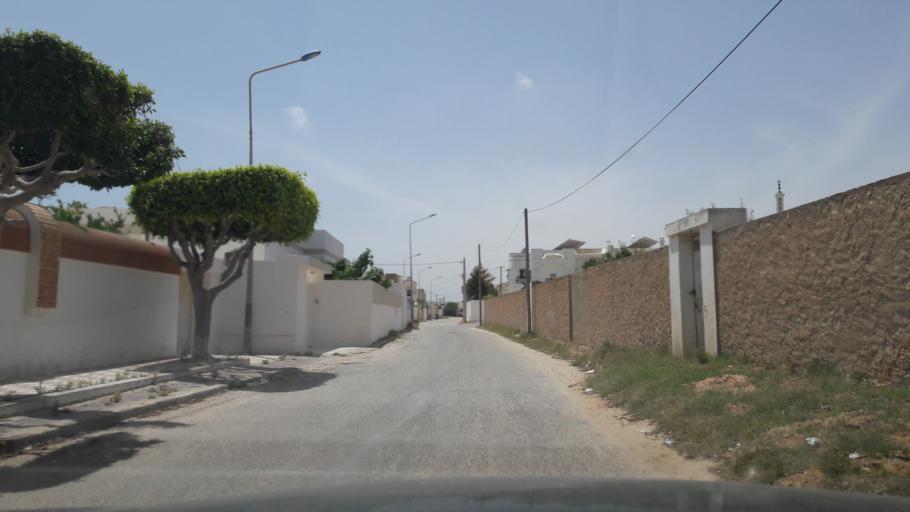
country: TN
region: Safaqis
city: Sfax
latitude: 34.7771
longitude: 10.7571
